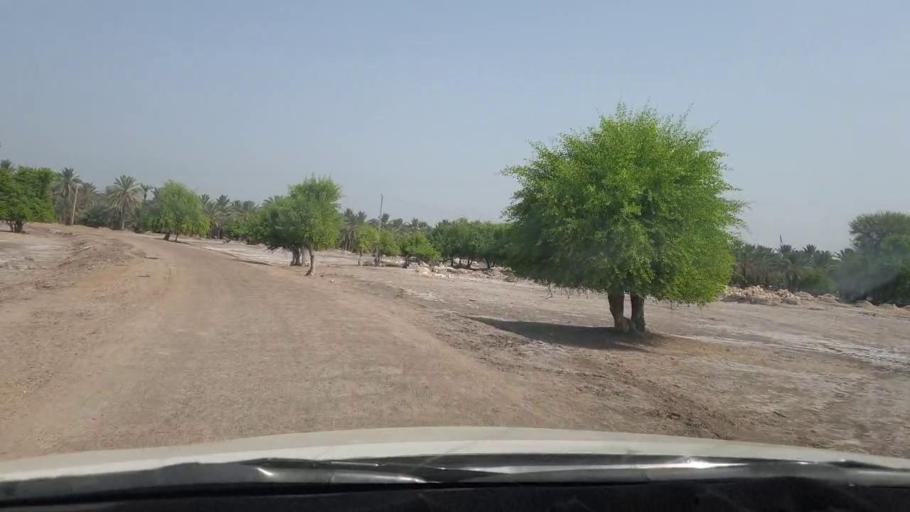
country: PK
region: Sindh
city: Rohri
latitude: 27.6251
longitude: 68.8882
